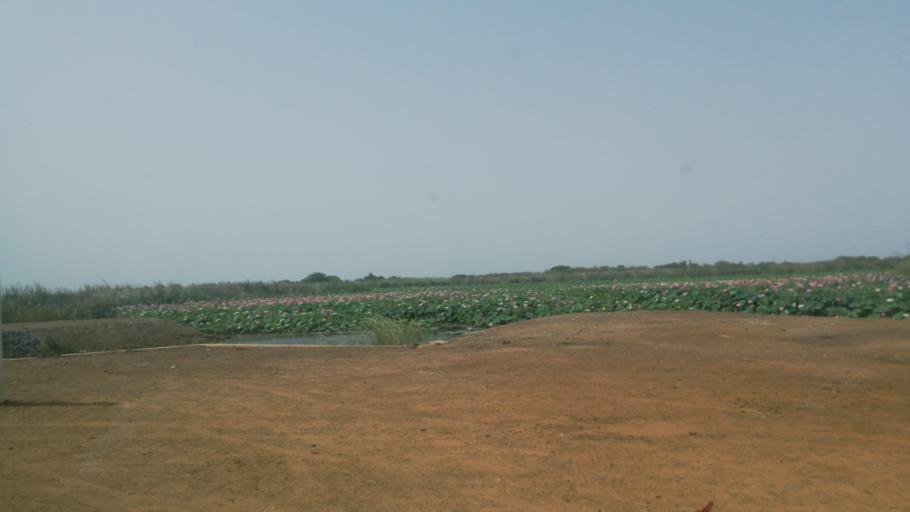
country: SN
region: Saint-Louis
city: Saint-Louis
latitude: 16.0649
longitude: -16.3187
